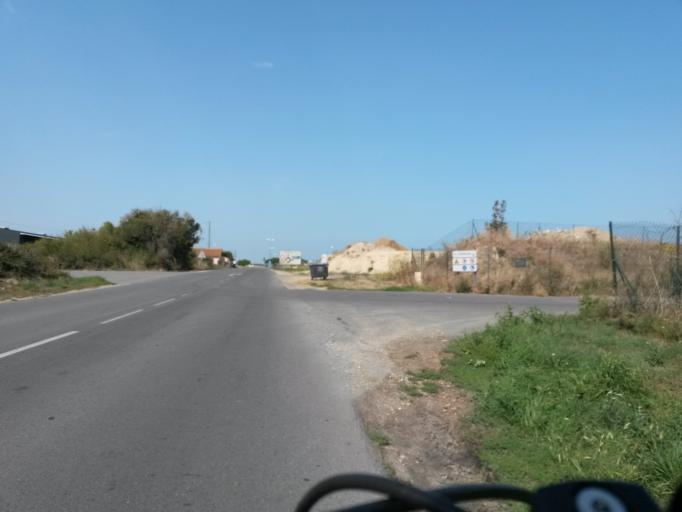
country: FR
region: Poitou-Charentes
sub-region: Departement de la Charente-Maritime
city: Rivedoux-Plage
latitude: 46.1721
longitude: -1.2144
